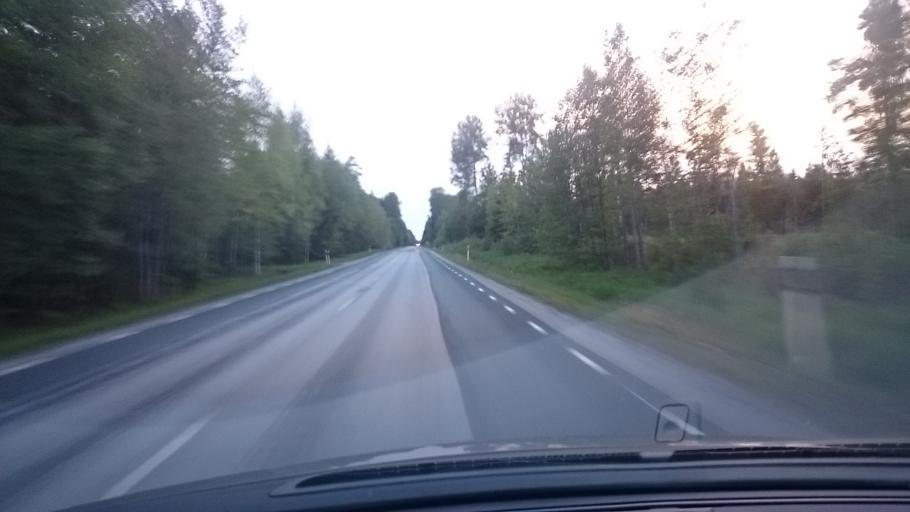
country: EE
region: Paernumaa
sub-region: Vaendra vald (alev)
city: Vandra
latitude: 58.8280
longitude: 25.1134
